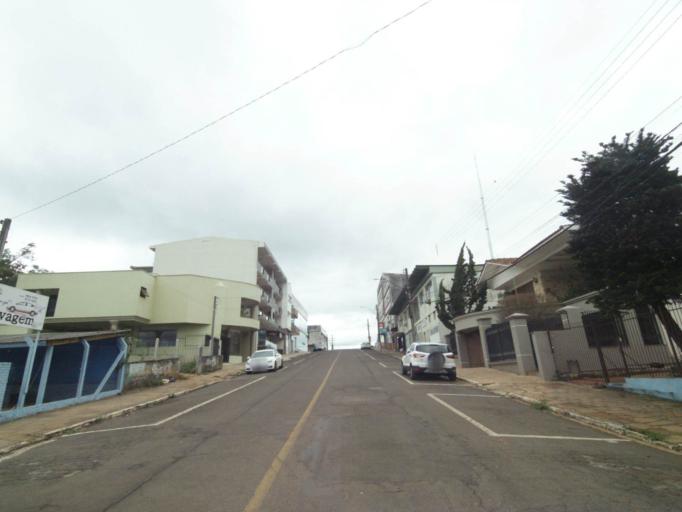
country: BR
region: Rio Grande do Sul
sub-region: Lagoa Vermelha
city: Lagoa Vermelha
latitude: -28.2095
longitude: -51.5282
